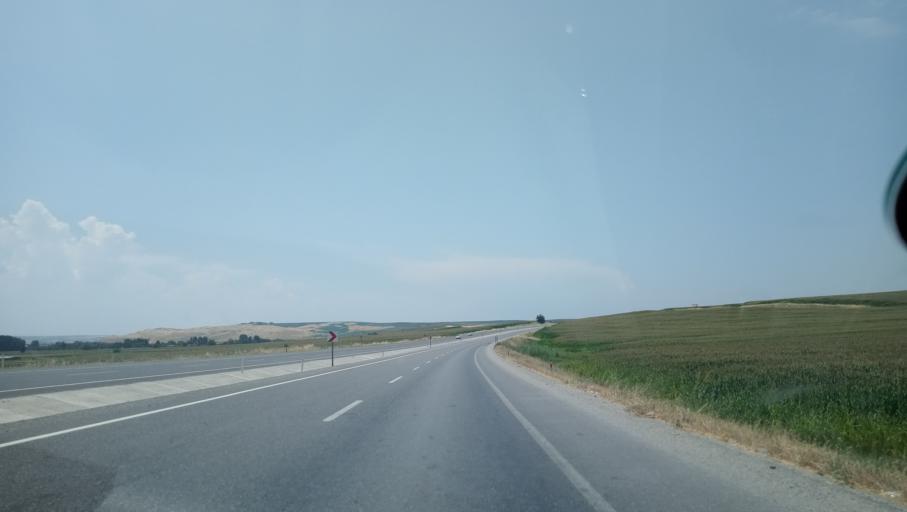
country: TR
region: Diyarbakir
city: Salat
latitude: 37.8467
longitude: 40.8415
